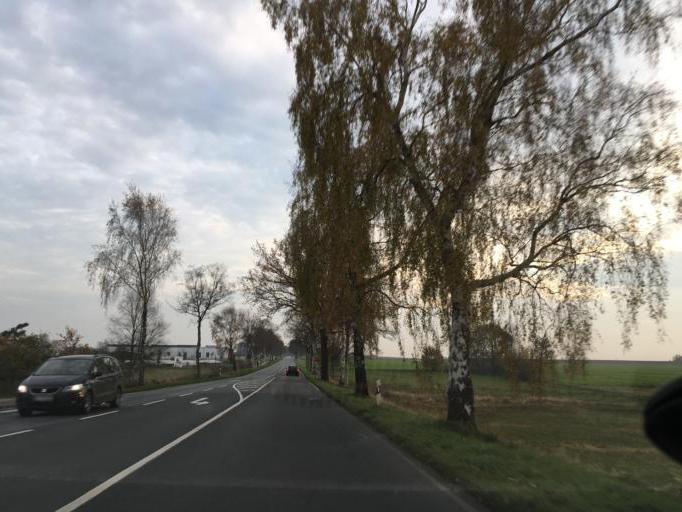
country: DE
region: Lower Saxony
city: Bergen
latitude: 52.7998
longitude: 9.9690
